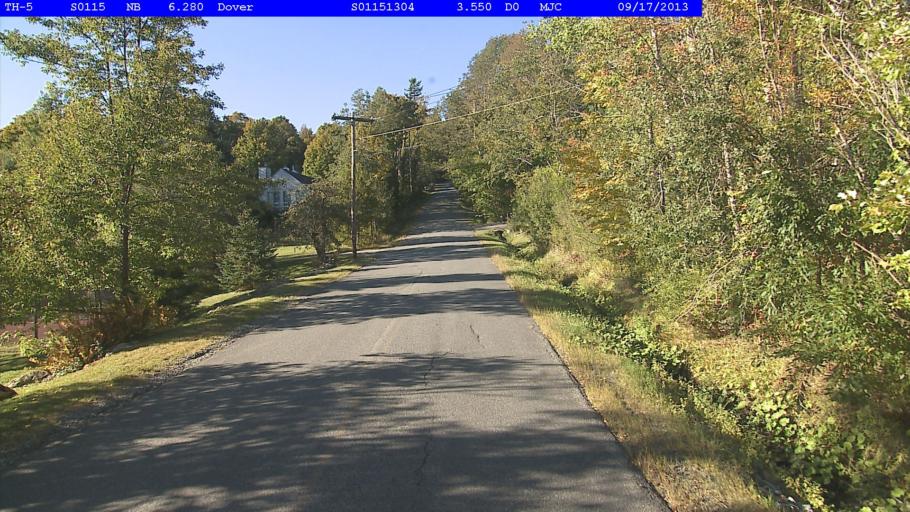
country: US
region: Vermont
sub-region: Windham County
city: Dover
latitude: 42.9745
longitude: -72.8923
